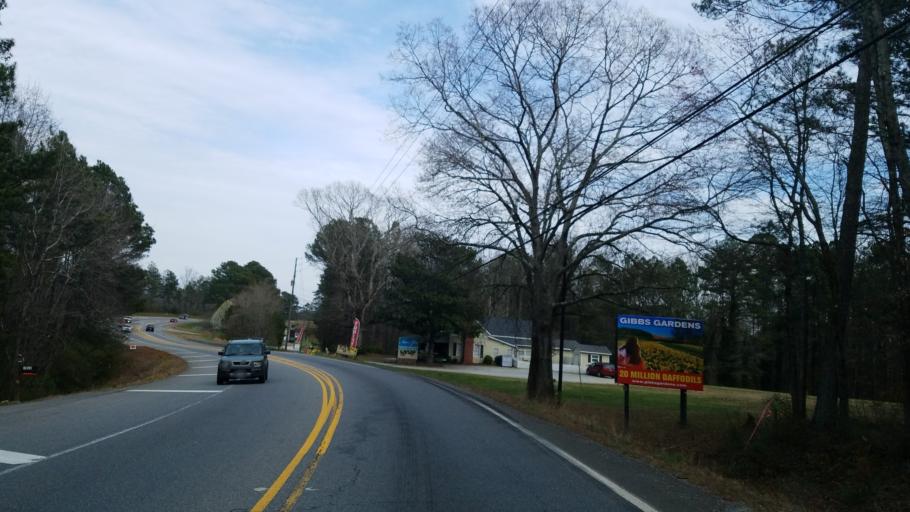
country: US
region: Georgia
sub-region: Cherokee County
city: Ball Ground
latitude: 34.2546
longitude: -84.3450
